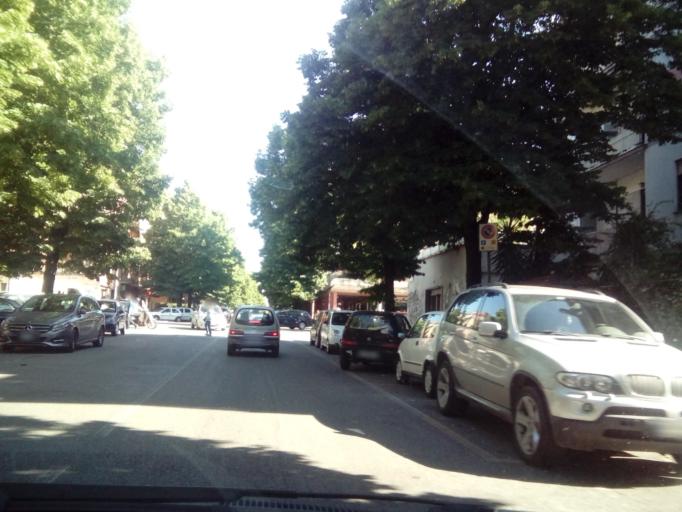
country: IT
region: Latium
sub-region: Citta metropolitana di Roma Capitale
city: Rome
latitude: 41.8922
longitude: 12.5660
